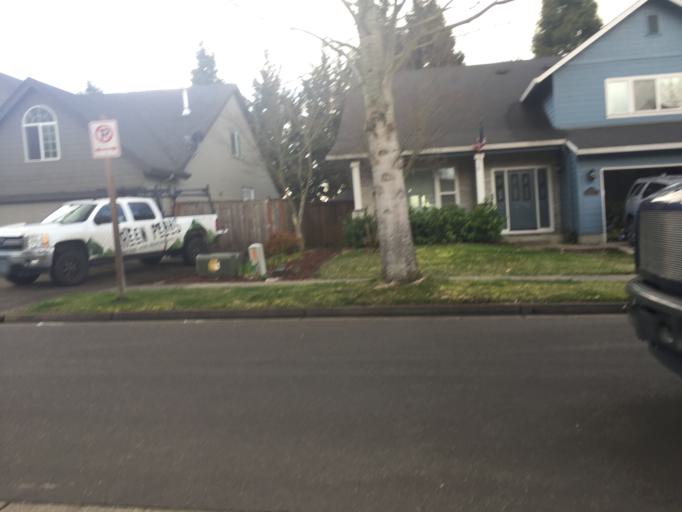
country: US
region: Oregon
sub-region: Lane County
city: Eugene
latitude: 44.1009
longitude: -123.1563
